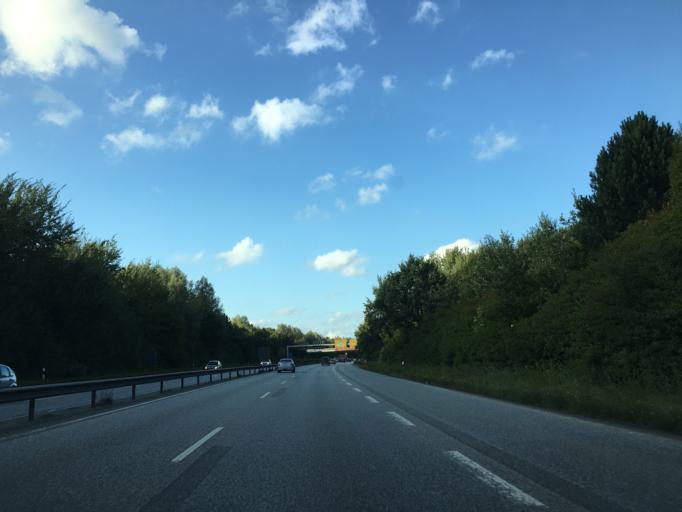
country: DE
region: Schleswig-Holstein
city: Kronshagen
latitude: 54.3222
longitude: 10.0979
